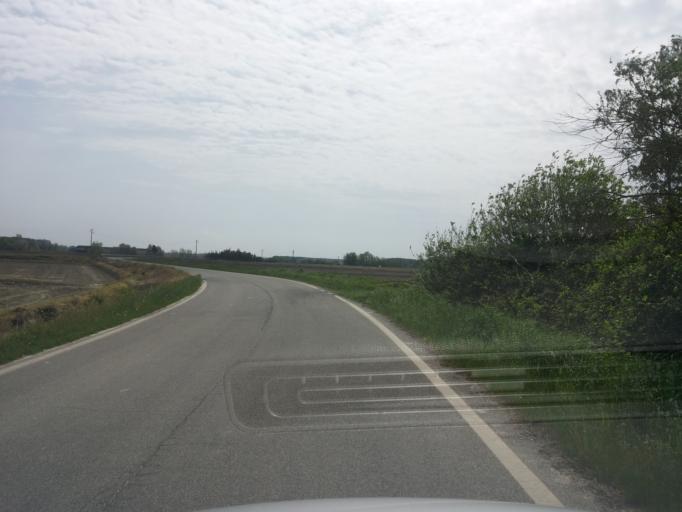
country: IT
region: Piedmont
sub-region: Provincia di Vercelli
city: Caresana
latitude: 45.2087
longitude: 8.5110
